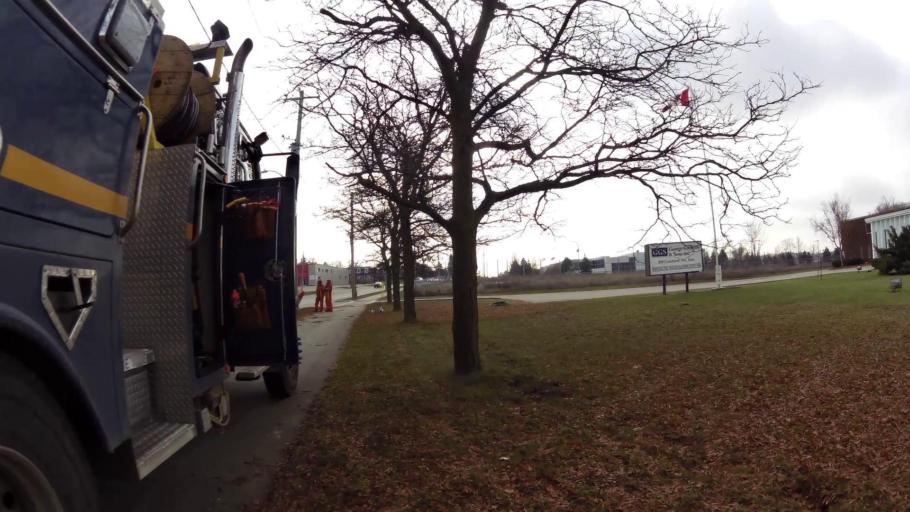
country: CA
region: Ontario
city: Kitchener
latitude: 43.4279
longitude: -80.4673
